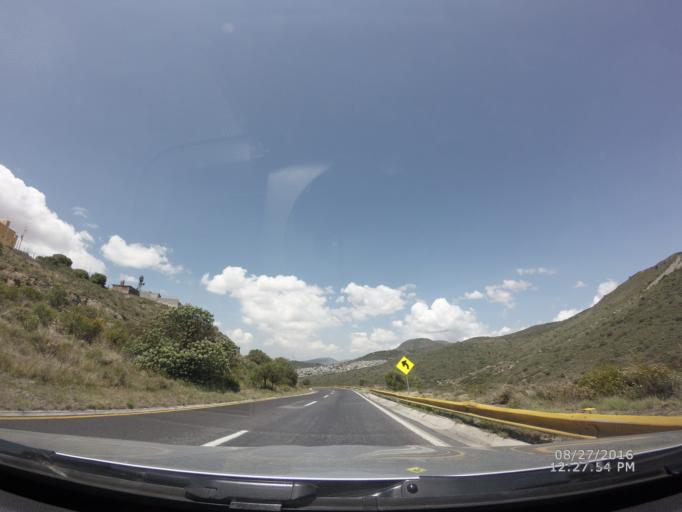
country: MX
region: Hidalgo
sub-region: Mineral de la Reforma
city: Colonia Militar
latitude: 20.1213
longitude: -98.6982
